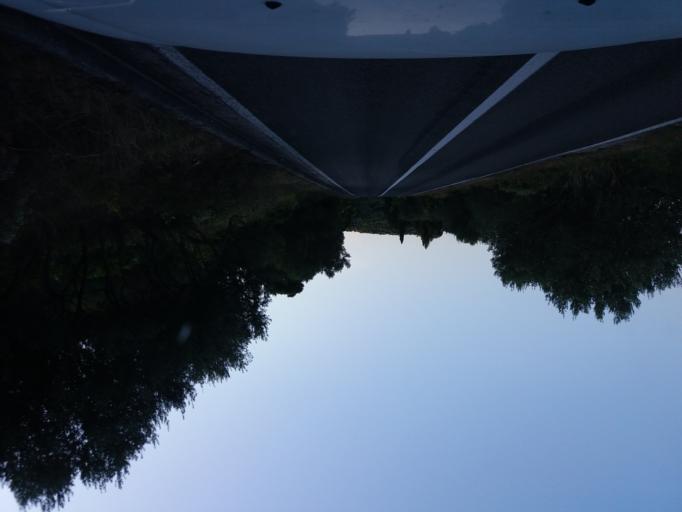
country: HR
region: Zadarska
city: Ugljan
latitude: 44.0803
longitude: 15.0014
